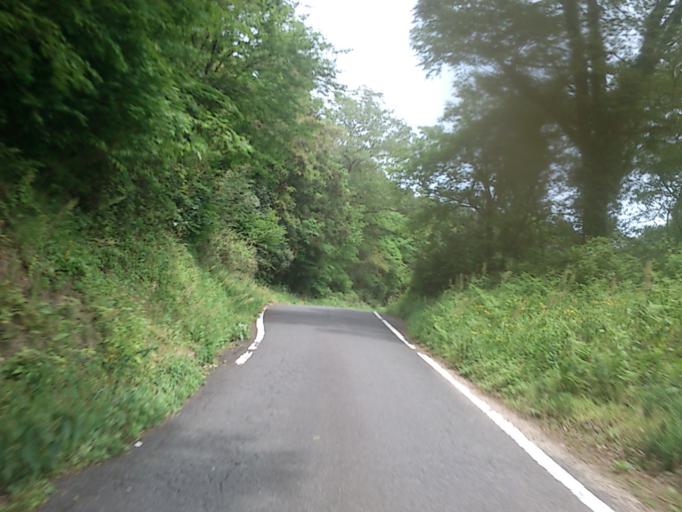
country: JP
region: Kyoto
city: Miyazu
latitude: 35.6076
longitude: 135.1104
